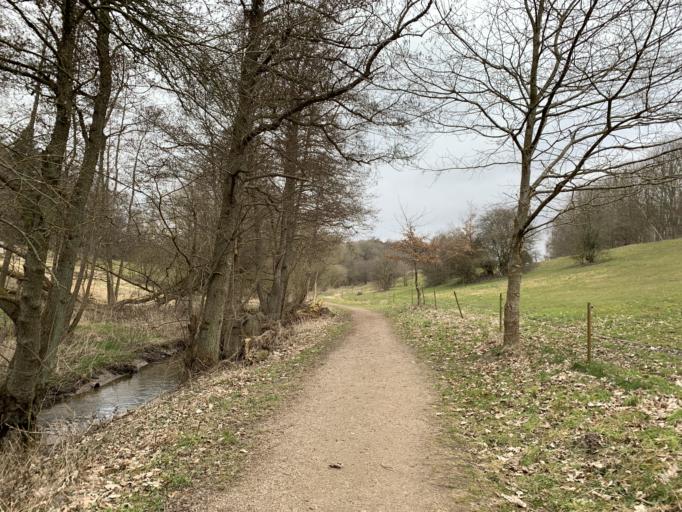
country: DK
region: South Denmark
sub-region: Odense Kommune
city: Bellinge
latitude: 55.4091
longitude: 10.3112
